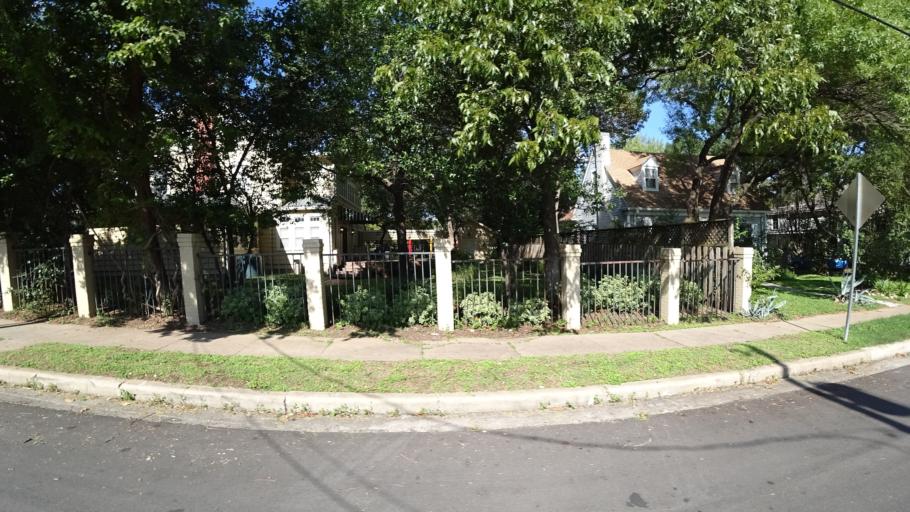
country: US
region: Texas
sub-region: Travis County
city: Austin
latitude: 30.3003
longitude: -97.7430
